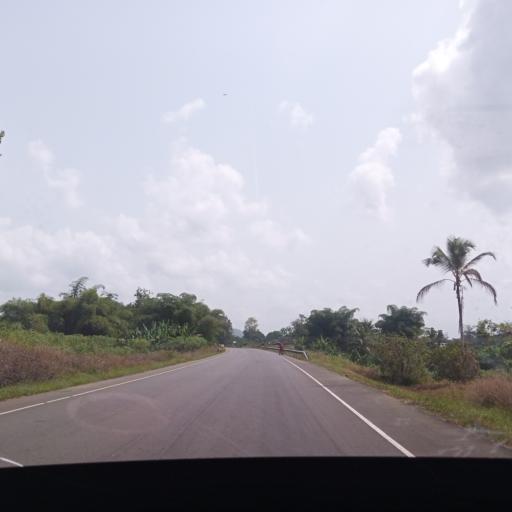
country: LR
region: Margibi
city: Kakata
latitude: 6.2511
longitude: -10.2989
